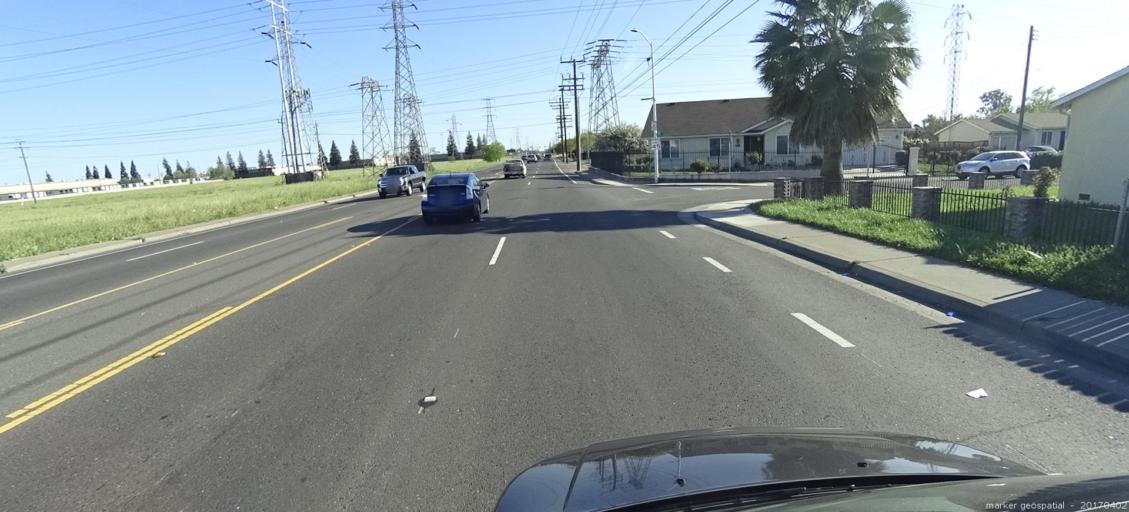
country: US
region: California
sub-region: Sacramento County
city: Florin
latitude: 38.5097
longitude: -121.4092
